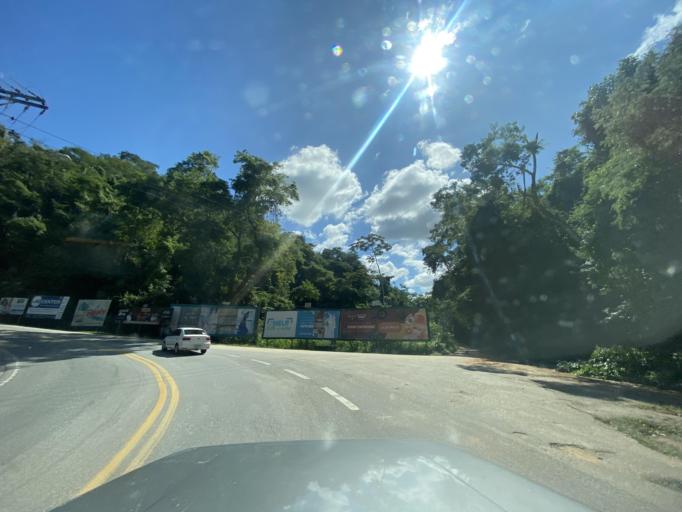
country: BR
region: Espirito Santo
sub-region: Alegre
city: Alegre
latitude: -20.7598
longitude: -41.5224
